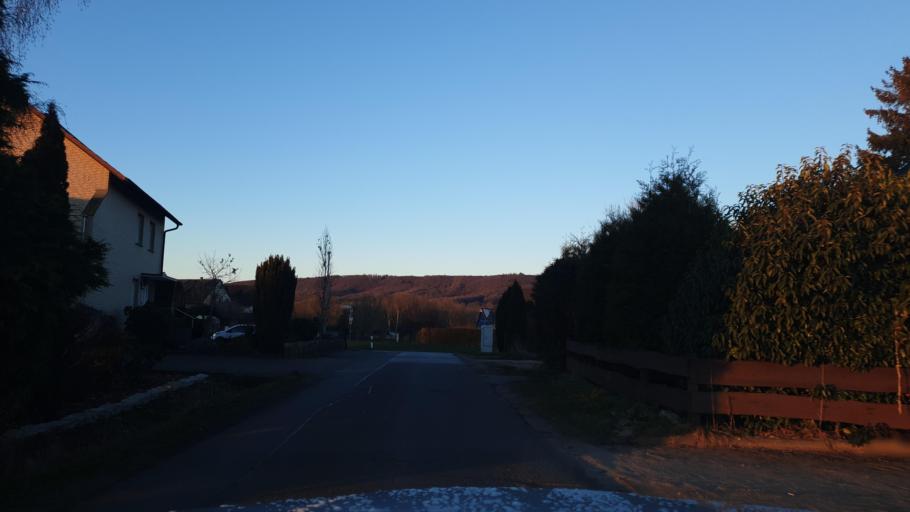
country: DE
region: North Rhine-Westphalia
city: Bad Oeynhausen
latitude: 52.2359
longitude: 8.8233
